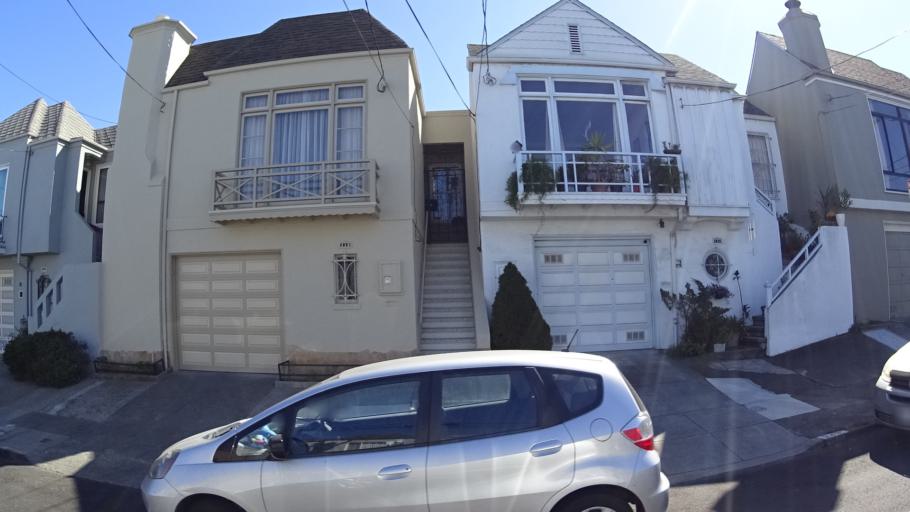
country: US
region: California
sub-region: San Francisco County
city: San Francisco
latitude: 37.7318
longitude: -122.4120
